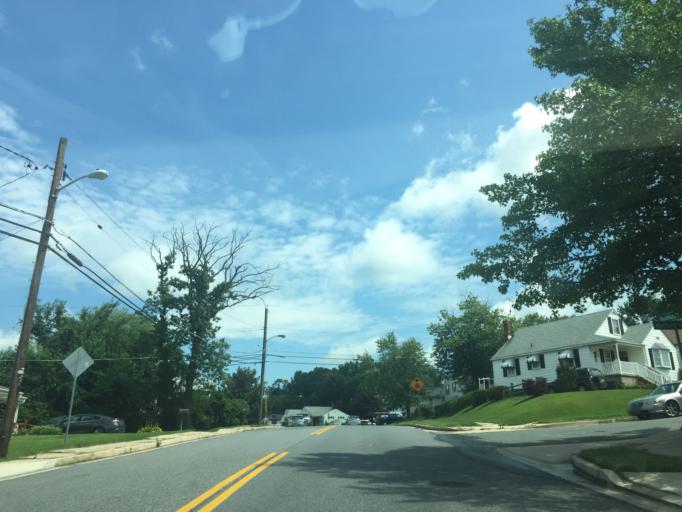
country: US
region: Maryland
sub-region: Baltimore County
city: Carney
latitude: 39.3884
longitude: -76.5217
